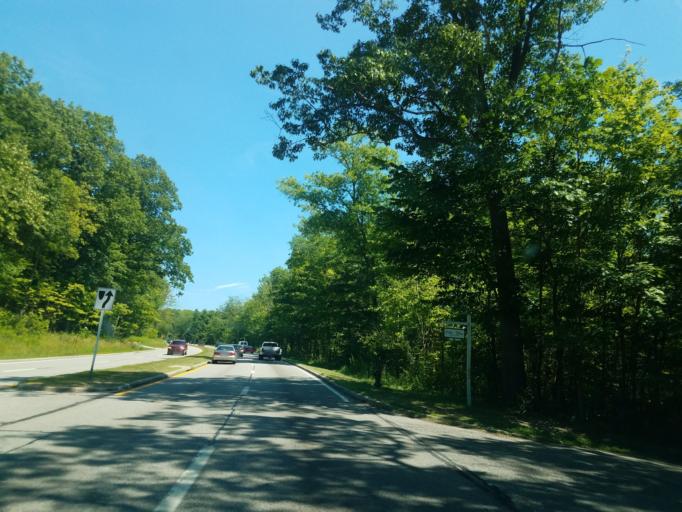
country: US
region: Ohio
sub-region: Cuyahoga County
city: Gates Mills
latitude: 41.5238
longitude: -81.3969
